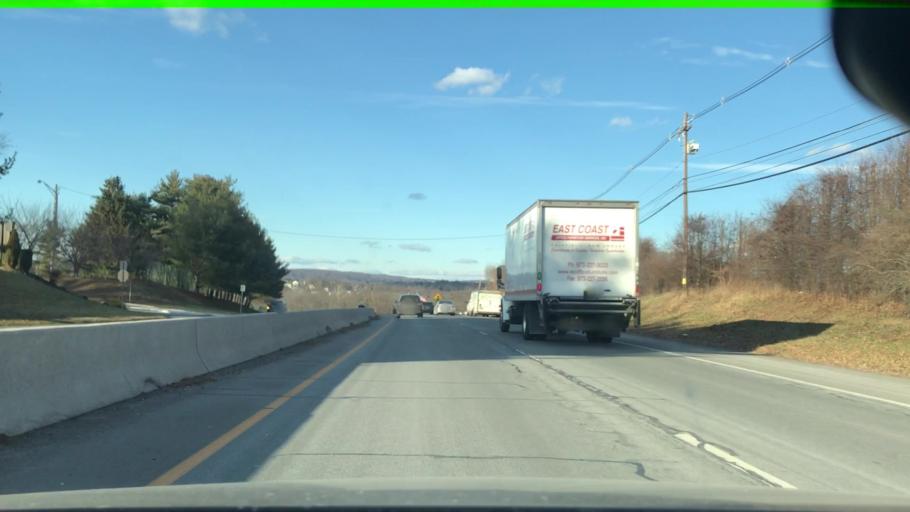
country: US
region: New Jersey
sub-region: Hunterdon County
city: Annandale
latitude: 40.6287
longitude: -74.8813
